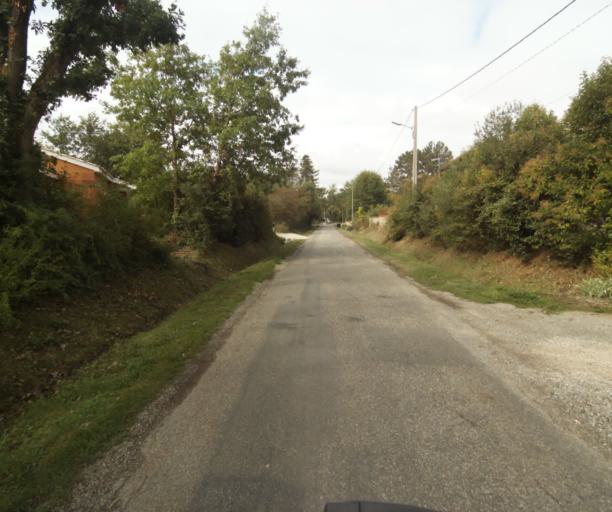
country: FR
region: Midi-Pyrenees
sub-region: Departement du Tarn-et-Garonne
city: Montech
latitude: 43.9558
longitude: 1.2482
